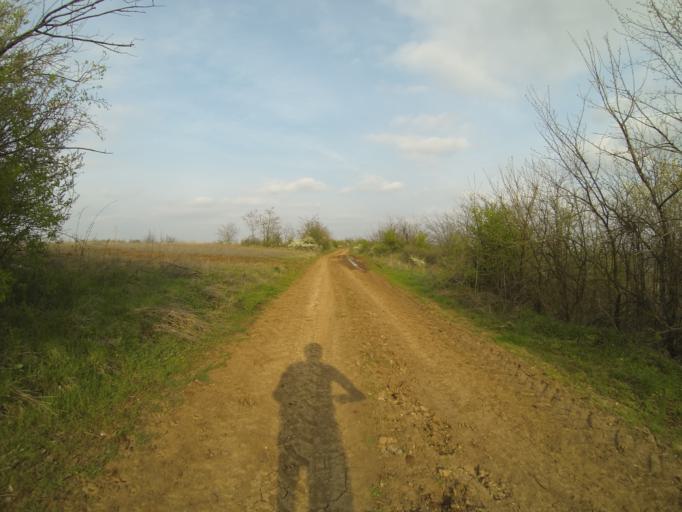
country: RO
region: Dolj
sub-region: Comuna Podari
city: Podari
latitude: 44.2473
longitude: 23.7549
